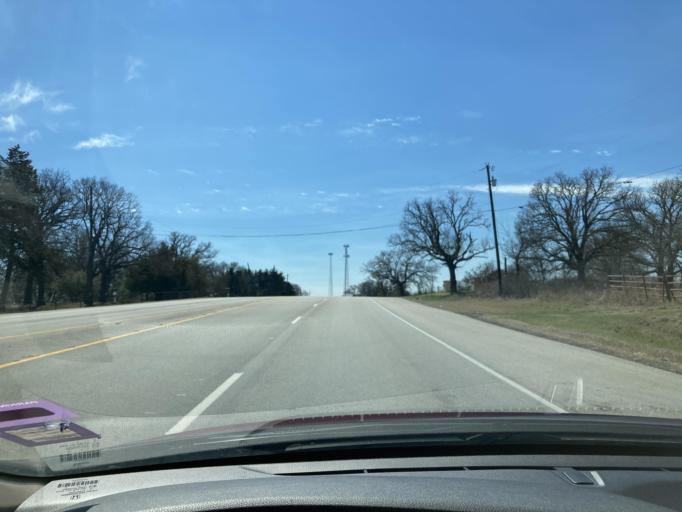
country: US
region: Texas
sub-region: Navarro County
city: Corsicana
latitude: 32.1400
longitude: -96.4682
